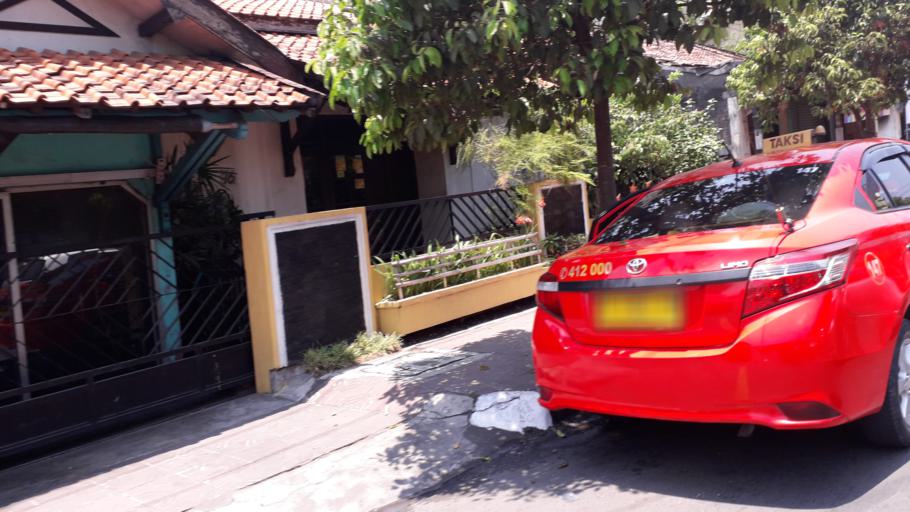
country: ID
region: Daerah Istimewa Yogyakarta
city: Yogyakarta
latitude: -7.7729
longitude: 110.3682
